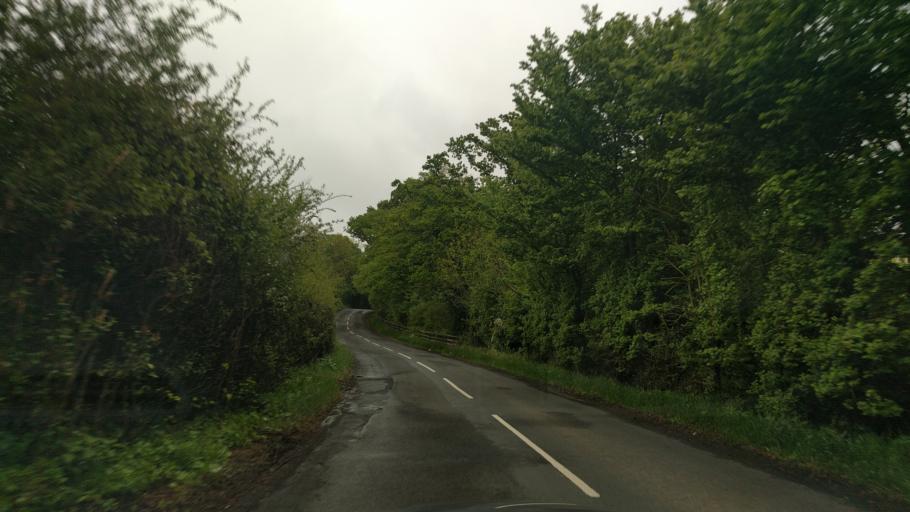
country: GB
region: England
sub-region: Northumberland
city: Morpeth
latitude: 55.1621
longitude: -1.7109
